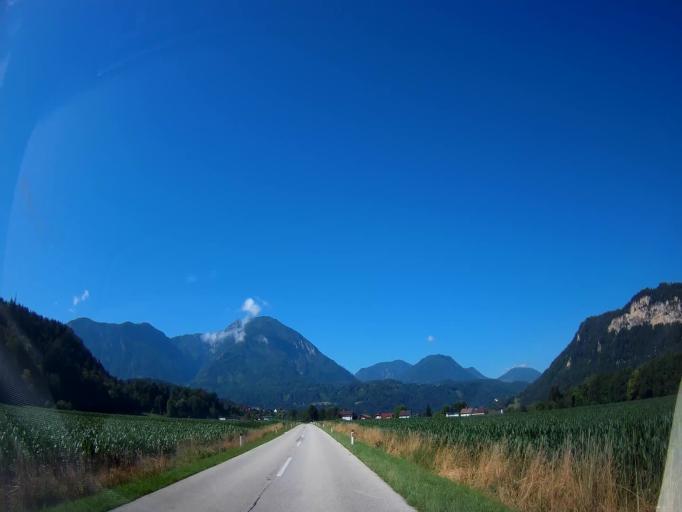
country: AT
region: Carinthia
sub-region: Politischer Bezirk Volkermarkt
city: Gallizien
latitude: 46.5840
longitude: 14.5133
